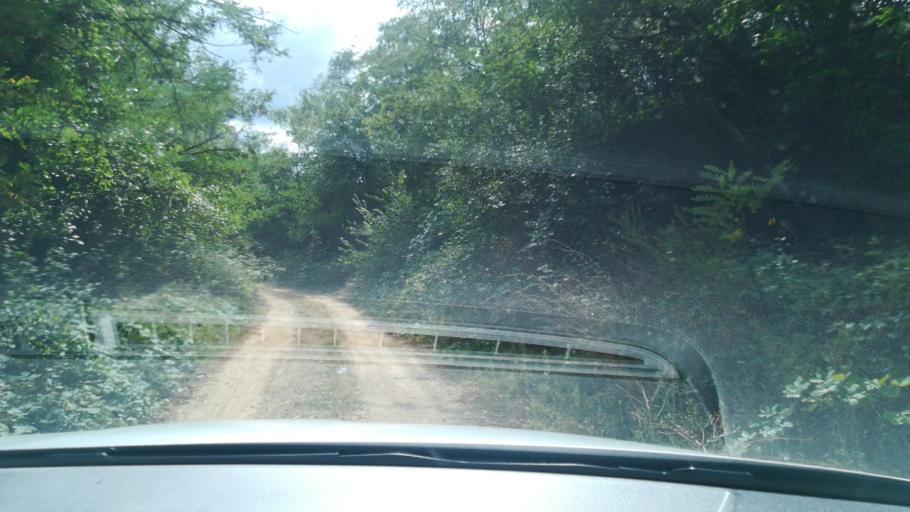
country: MK
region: Delcevo
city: Delcevo
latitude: 41.8924
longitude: 22.8048
